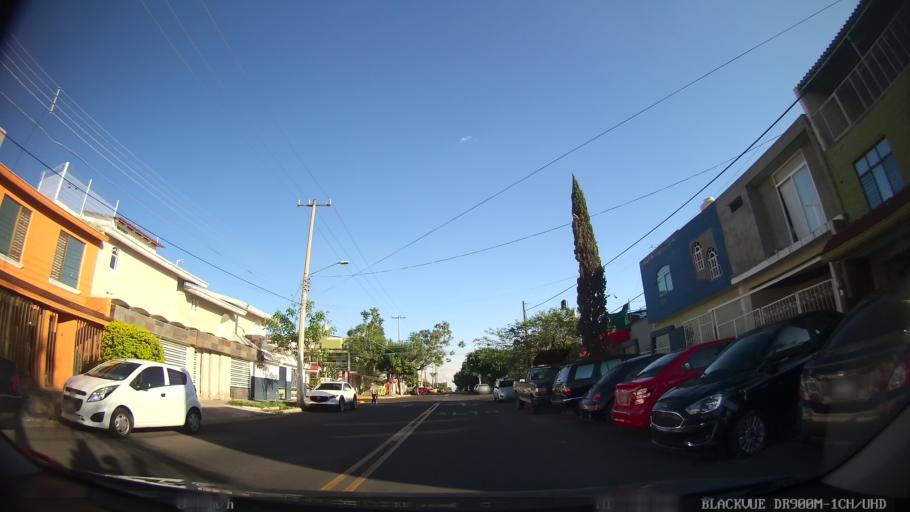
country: MX
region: Jalisco
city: Tlaquepaque
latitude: 20.7038
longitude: -103.2970
